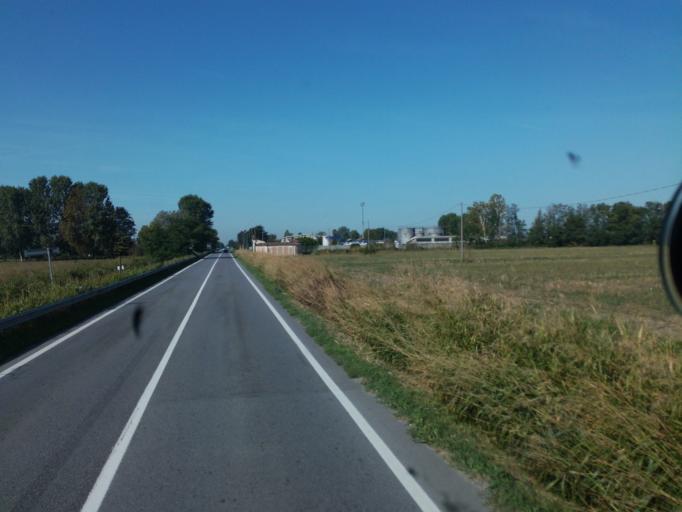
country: IT
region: Lombardy
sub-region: Provincia di Cremona
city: Capergnanica
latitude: 45.3535
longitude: 9.6346
